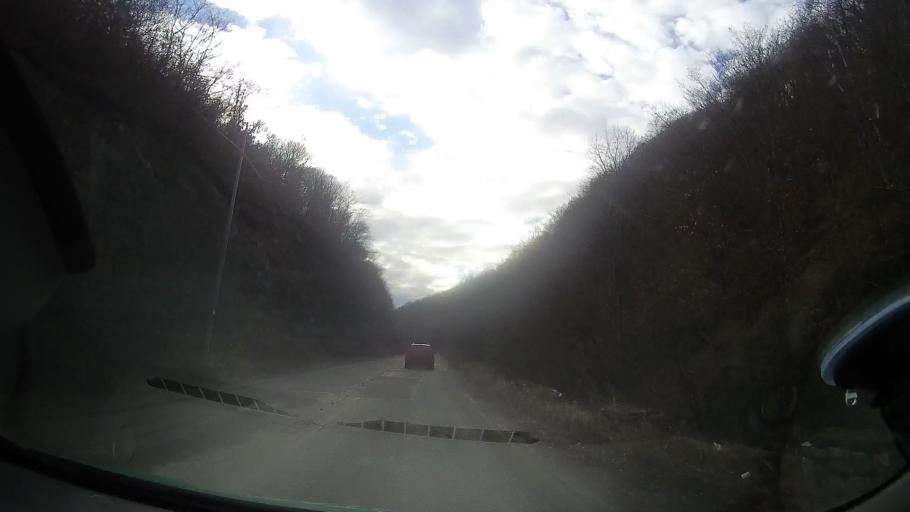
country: RO
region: Cluj
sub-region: Comuna Baisoara
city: Baisoara
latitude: 46.5902
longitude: 23.4586
